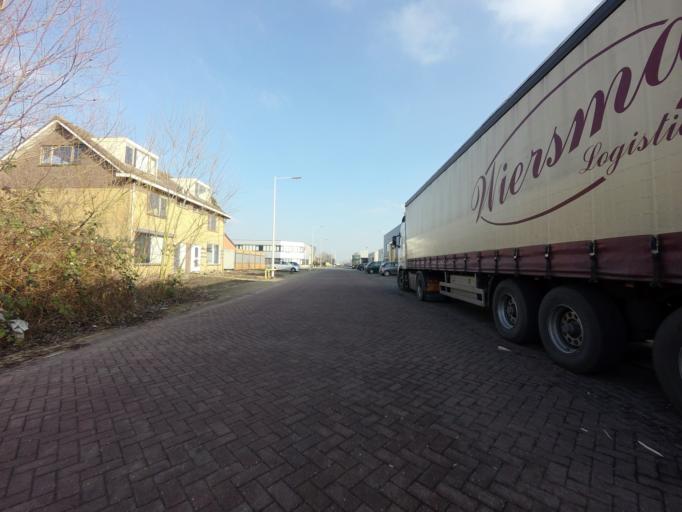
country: NL
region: Utrecht
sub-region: Gemeente Lopik
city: Lopik
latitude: 51.9830
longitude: 4.9718
